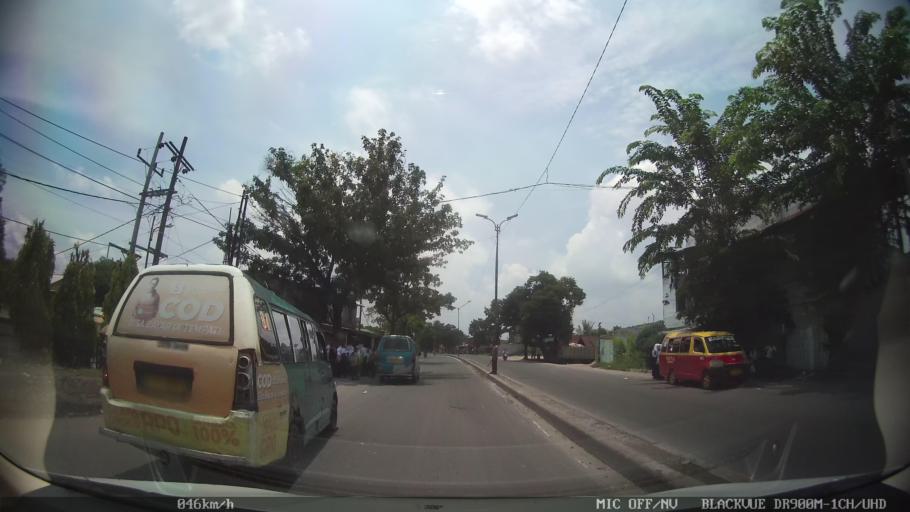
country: ID
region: North Sumatra
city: Labuhan Deli
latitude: 3.7162
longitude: 98.6798
